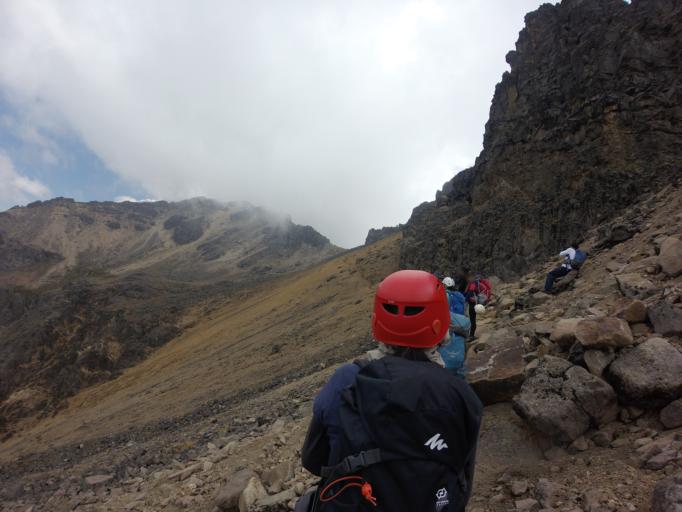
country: MX
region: Mexico
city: Amecameca de Juarez
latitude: 19.1459
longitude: -98.6386
